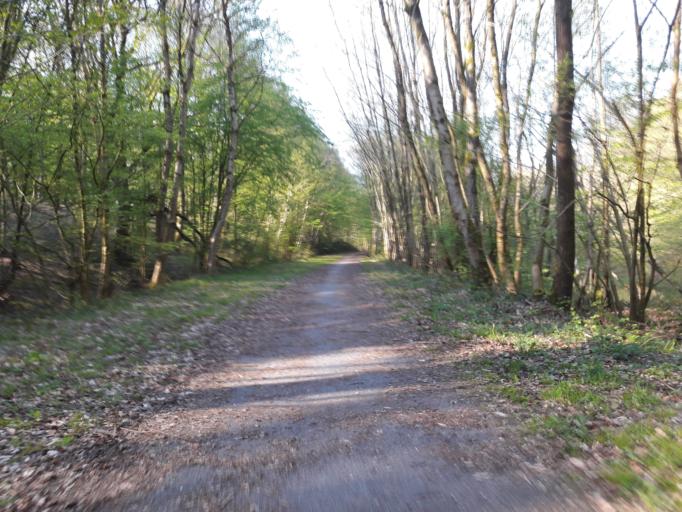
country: FR
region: Nord-Pas-de-Calais
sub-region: Departement du Nord
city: Sains-du-Nord
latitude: 50.1372
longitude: 4.0662
